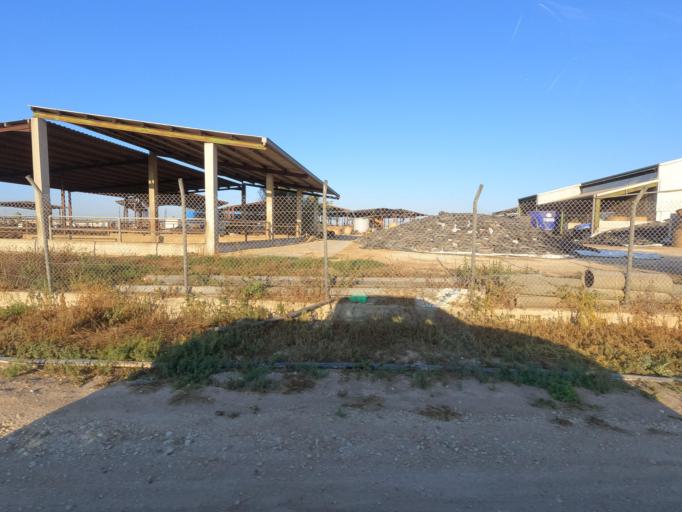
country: CY
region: Ammochostos
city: Achna
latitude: 35.0359
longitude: 33.7881
